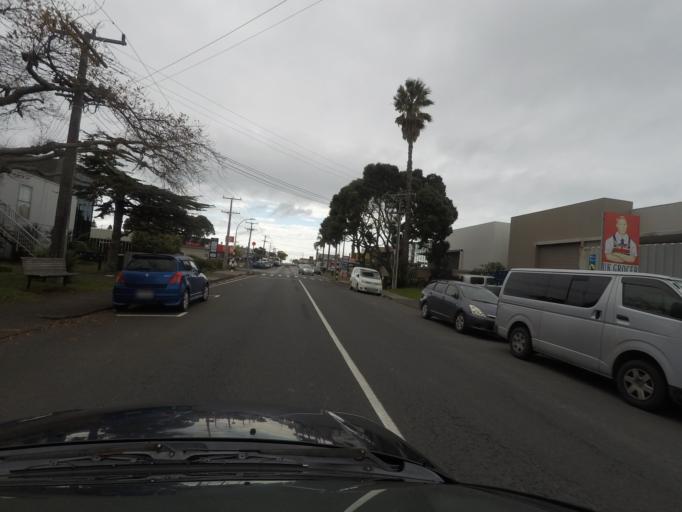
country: NZ
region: Auckland
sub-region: Auckland
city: Rothesay Bay
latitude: -36.7168
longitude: 174.7448
